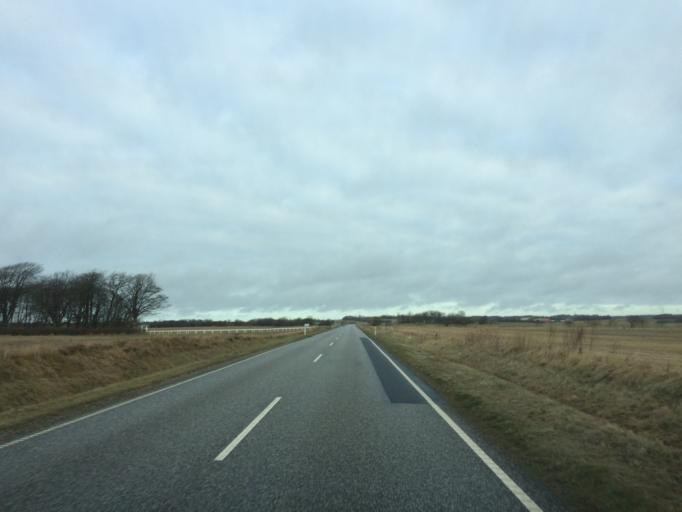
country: DK
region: Central Jutland
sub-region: Struer Kommune
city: Struer
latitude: 56.4005
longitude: 8.4618
